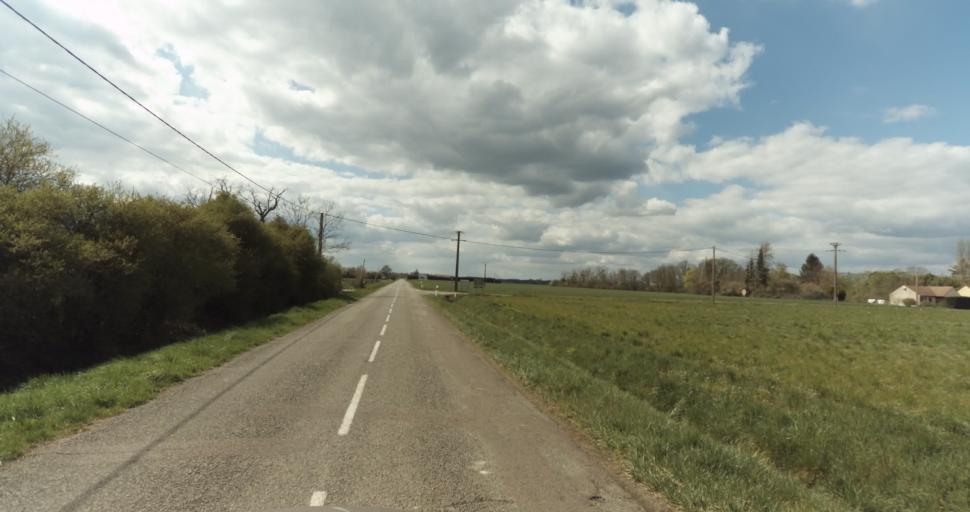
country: FR
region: Bourgogne
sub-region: Departement de la Cote-d'Or
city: Auxonne
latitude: 47.1950
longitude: 5.4253
